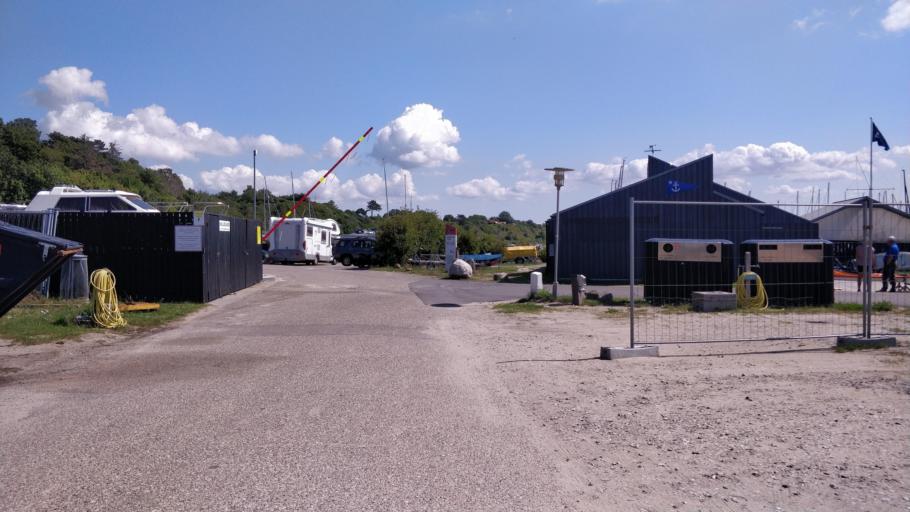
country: DK
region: Capital Region
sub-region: Halsnaes Kommune
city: Hundested
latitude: 55.9440
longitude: 11.8646
